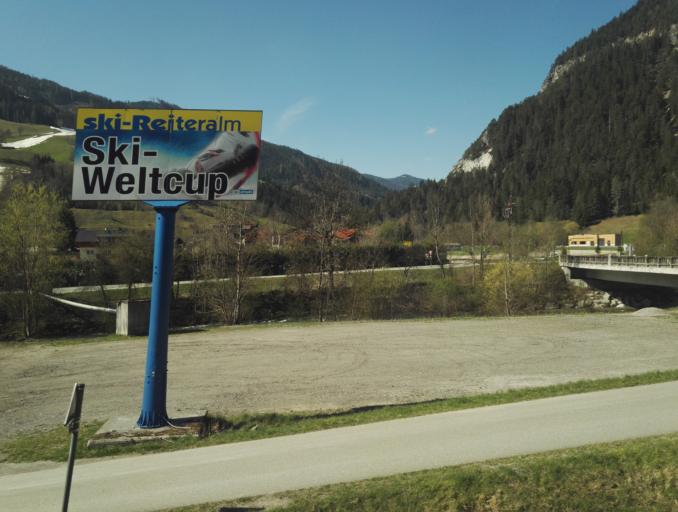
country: AT
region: Salzburg
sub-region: Politischer Bezirk Sankt Johann im Pongau
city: Forstau
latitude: 47.3905
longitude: 13.5965
